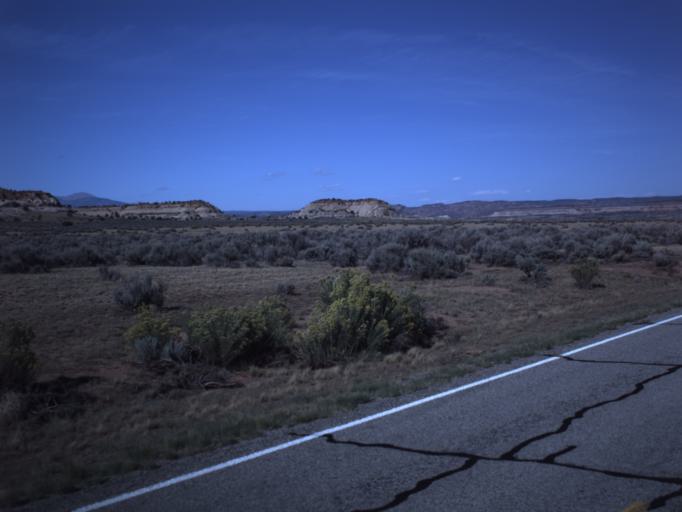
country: US
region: Utah
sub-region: San Juan County
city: Monticello
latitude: 38.0647
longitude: -109.3854
